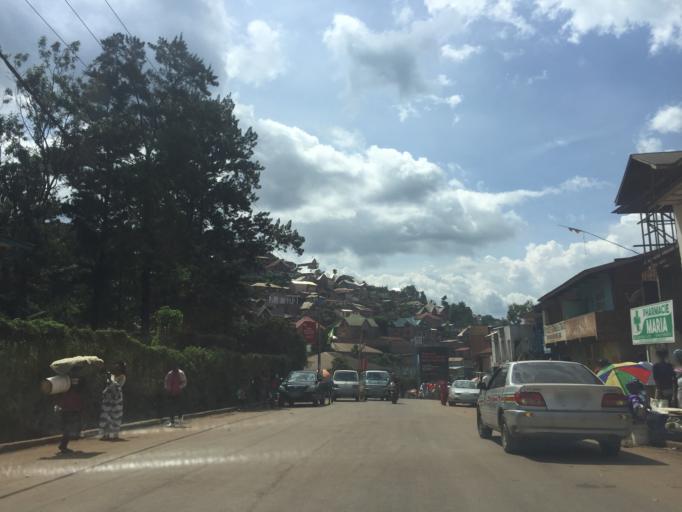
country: CD
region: South Kivu
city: Bukavu
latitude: -2.4944
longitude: 28.8501
